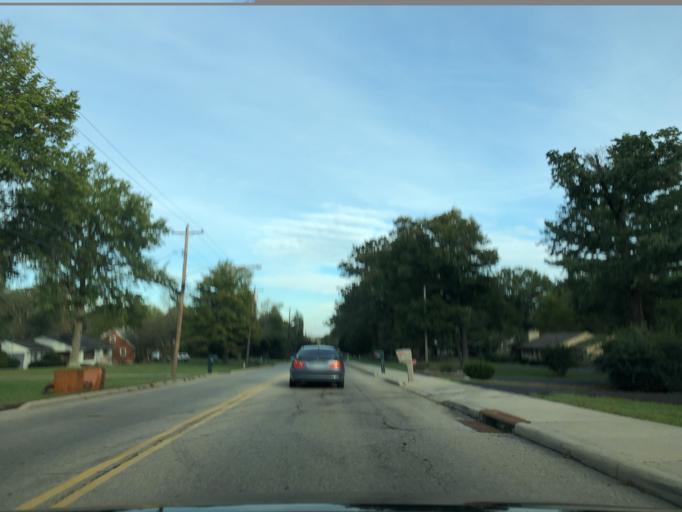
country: US
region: Ohio
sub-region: Hamilton County
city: Loveland
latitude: 39.2714
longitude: -84.2790
